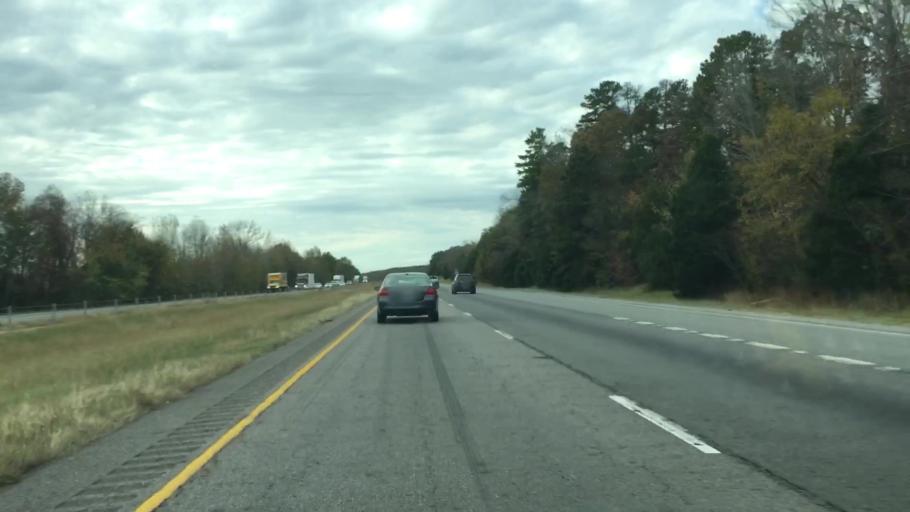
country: US
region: Arkansas
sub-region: Faulkner County
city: Conway
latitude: 35.1546
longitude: -92.5581
